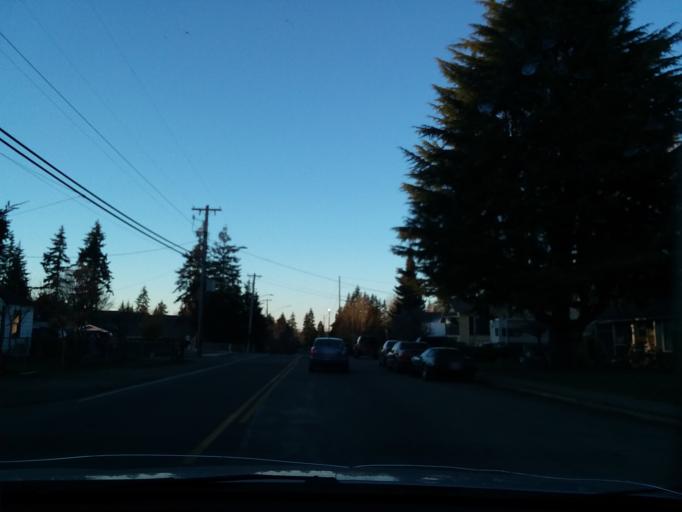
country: US
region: Washington
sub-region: Snohomish County
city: Mountlake Terrace
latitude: 47.8020
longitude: -122.2978
